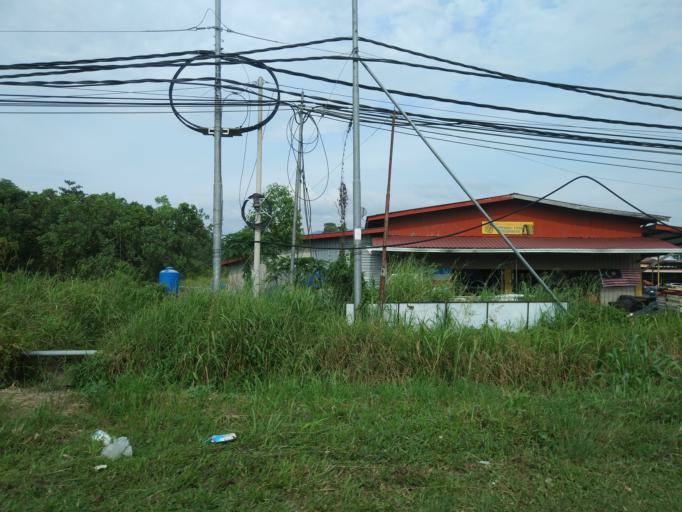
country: MY
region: Sabah
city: Beaufort
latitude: 5.0652
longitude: 115.5502
